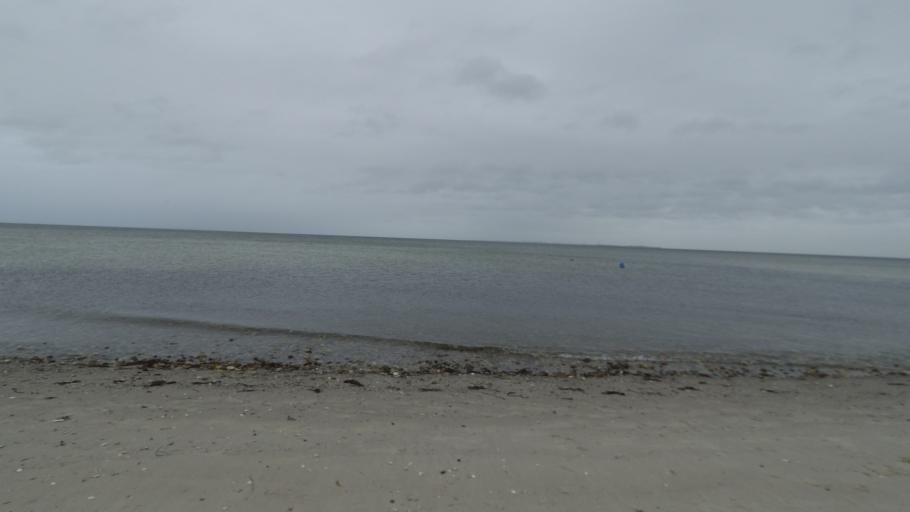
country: DK
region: Central Jutland
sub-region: Arhus Kommune
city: Malling
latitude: 55.9745
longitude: 10.2546
